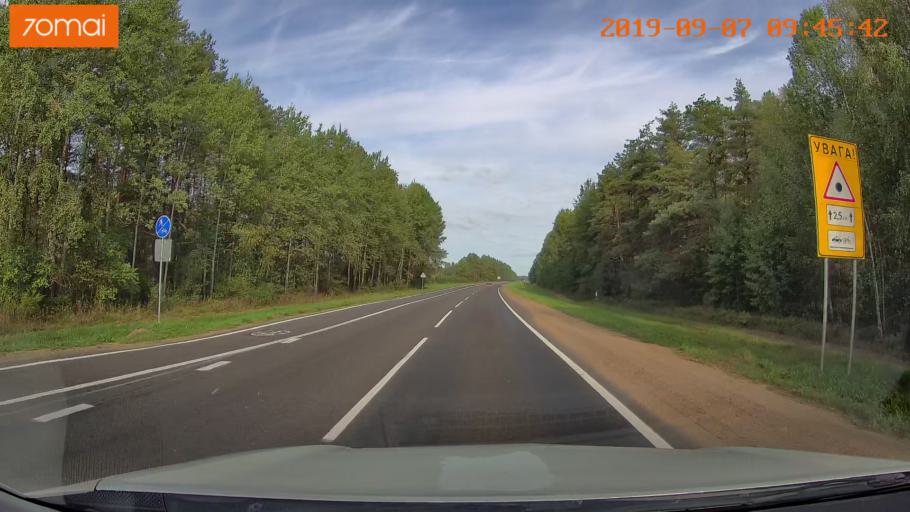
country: BY
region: Grodnenskaya
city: Iwye
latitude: 53.9564
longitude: 25.7289
